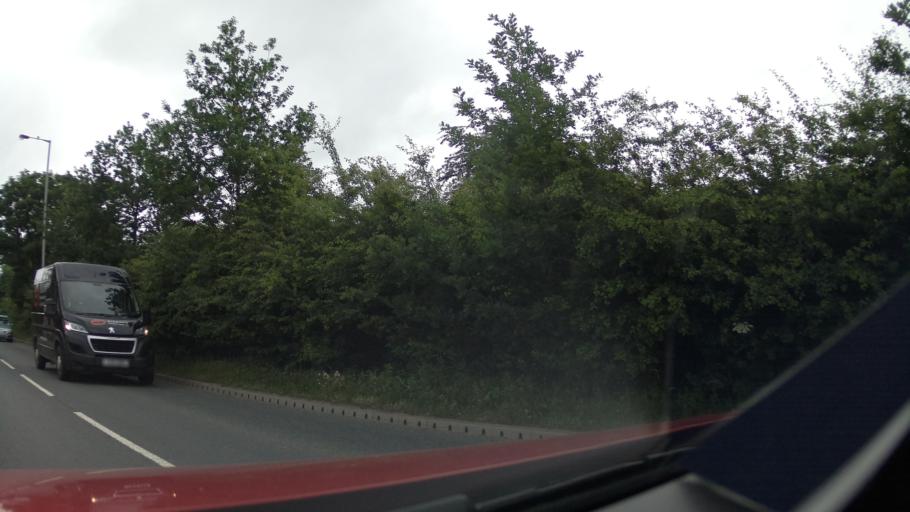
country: GB
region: England
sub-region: Staffordshire
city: Burton upon Trent
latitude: 52.8323
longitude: -1.6138
